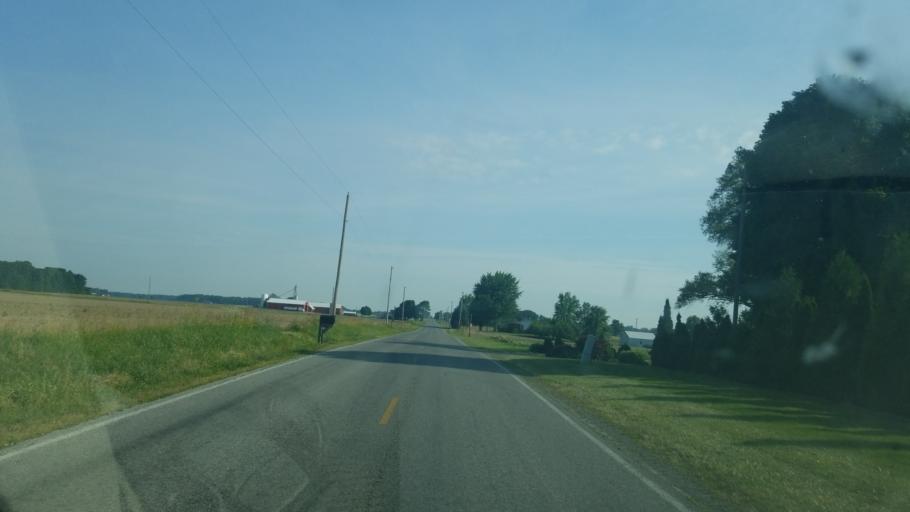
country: US
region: Ohio
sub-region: Hancock County
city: Arlington
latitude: 40.9192
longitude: -83.6986
